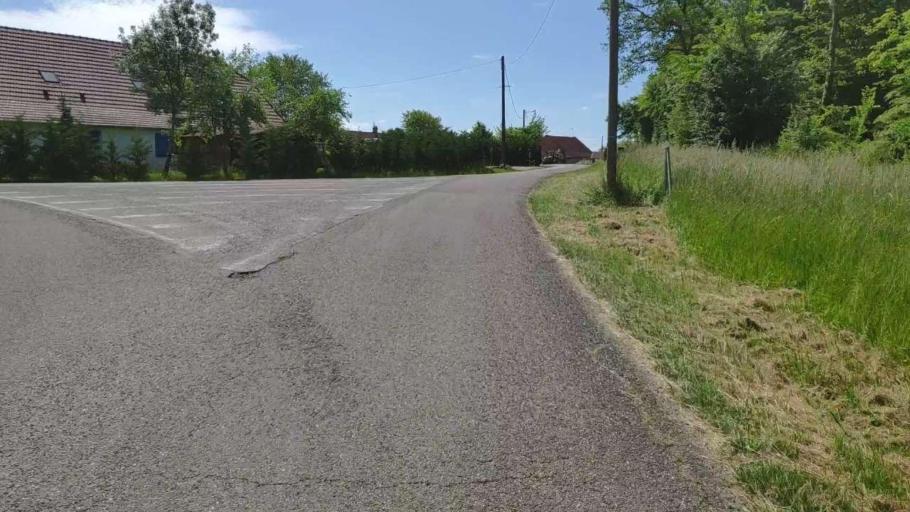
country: FR
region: Franche-Comte
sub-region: Departement du Jura
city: Bletterans
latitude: 46.7070
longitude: 5.4107
